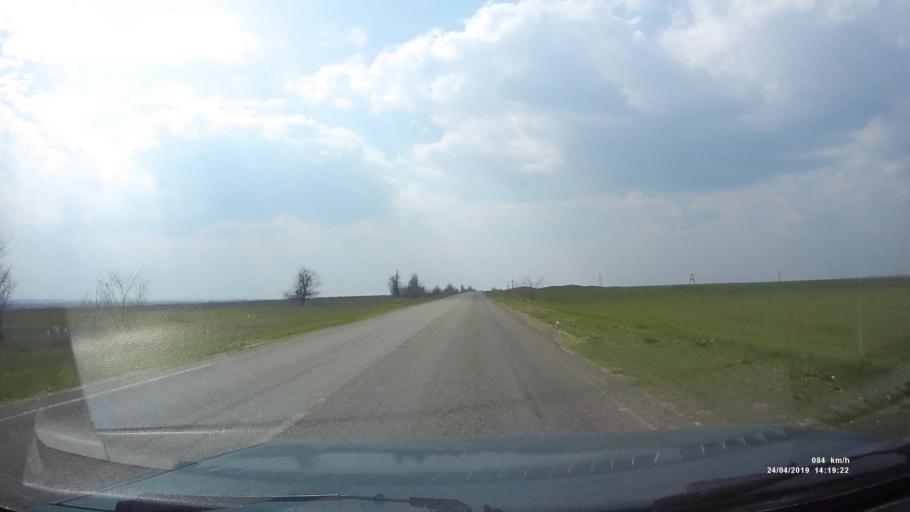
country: RU
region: Kalmykiya
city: Arshan'
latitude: 46.3053
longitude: 44.1769
